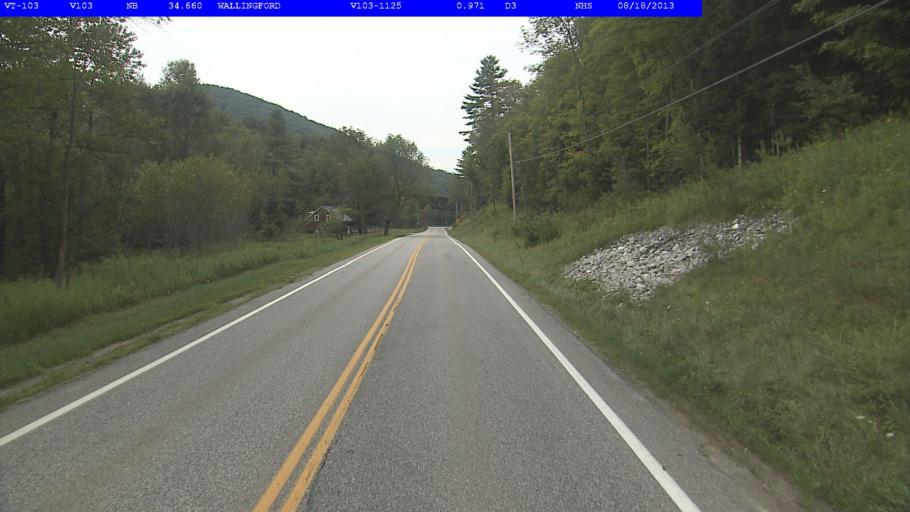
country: US
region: Vermont
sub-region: Rutland County
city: Rutland
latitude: 43.4605
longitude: -72.8795
